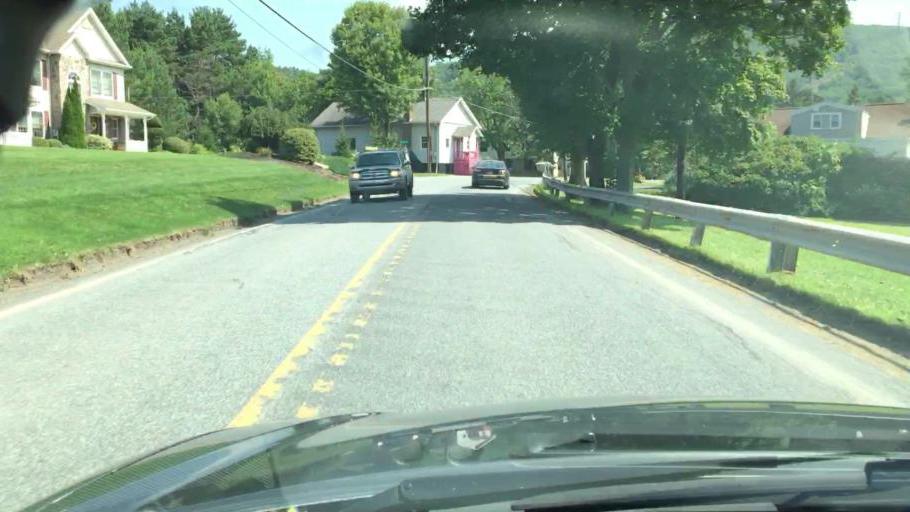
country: US
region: Pennsylvania
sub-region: Luzerne County
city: Harleigh
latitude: 41.0210
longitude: -75.9713
